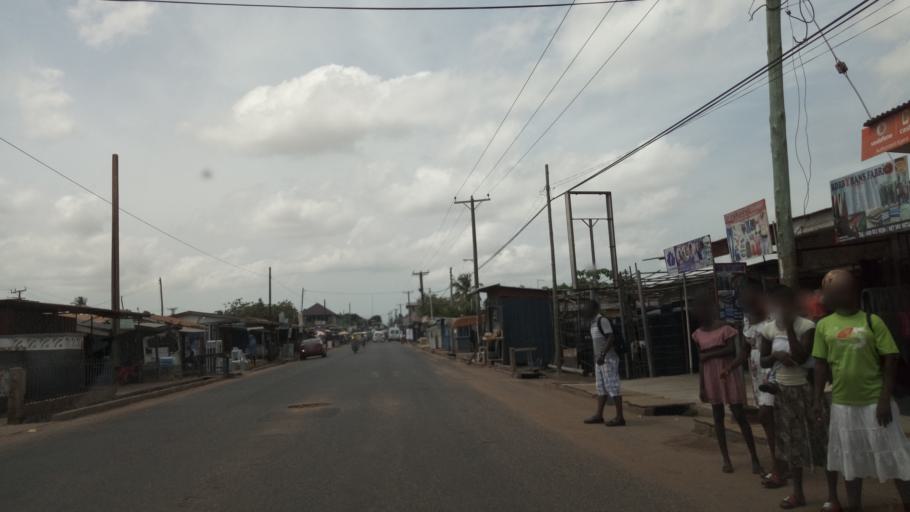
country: GH
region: Greater Accra
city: Medina Estates
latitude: 5.6819
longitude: -0.1605
